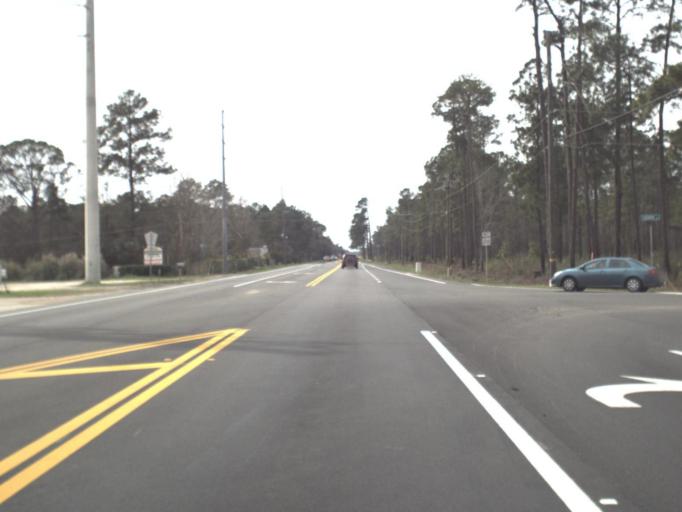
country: US
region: Florida
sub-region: Gadsden County
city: Midway
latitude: 30.4436
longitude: -84.4033
